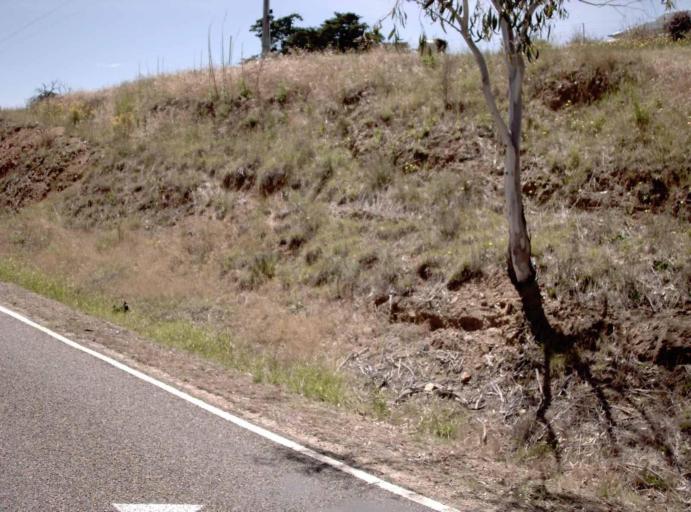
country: AU
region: Victoria
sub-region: Alpine
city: Mount Beauty
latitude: -37.1079
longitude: 147.5798
